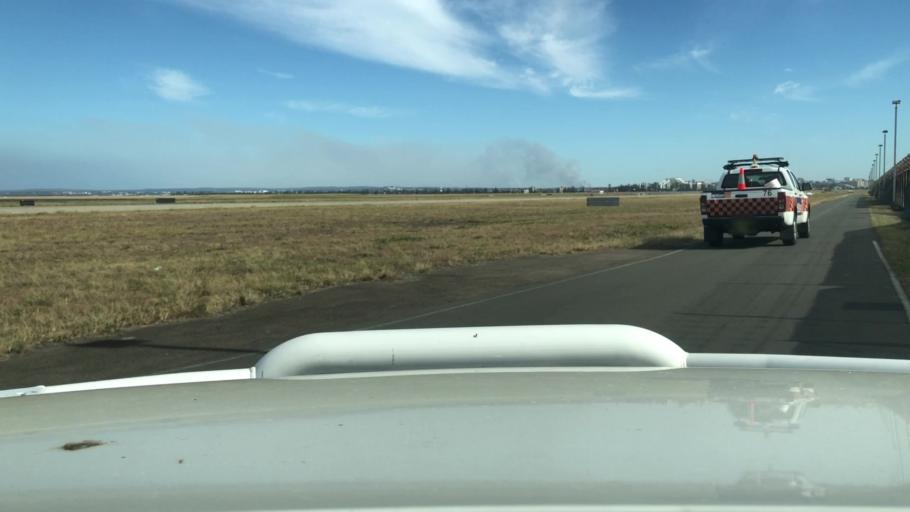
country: AU
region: New South Wales
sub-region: Botany Bay
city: Botany
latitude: -33.9498
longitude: 151.1852
